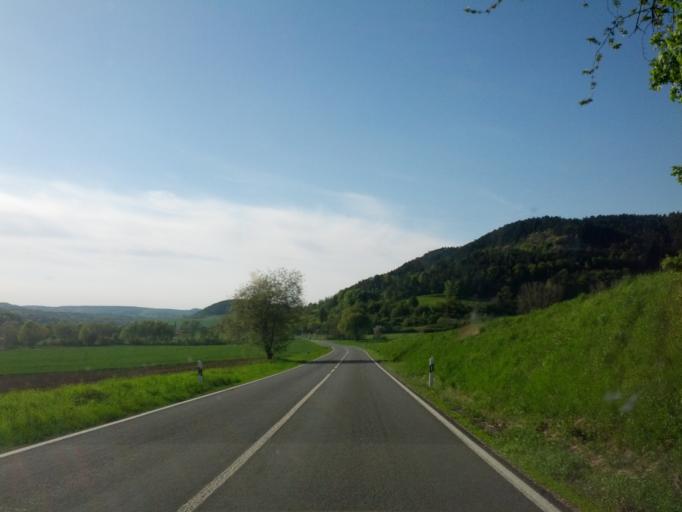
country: DE
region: Thuringia
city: Geismar
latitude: 51.2215
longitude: 10.1911
